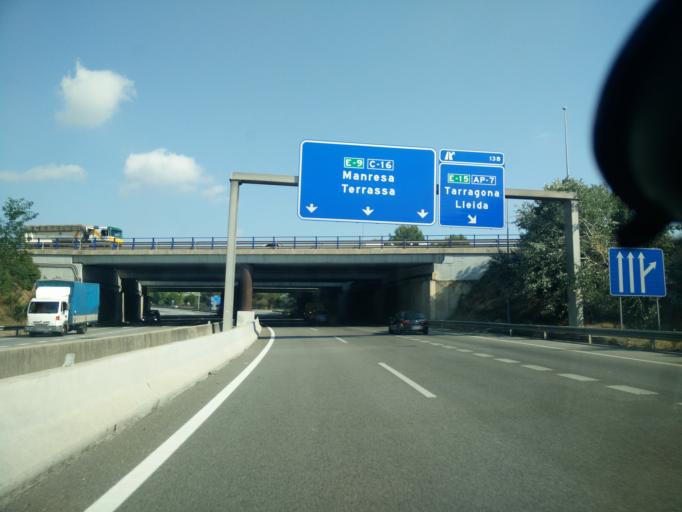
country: ES
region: Catalonia
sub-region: Provincia de Barcelona
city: Rubi
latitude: 41.4885
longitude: 2.0601
